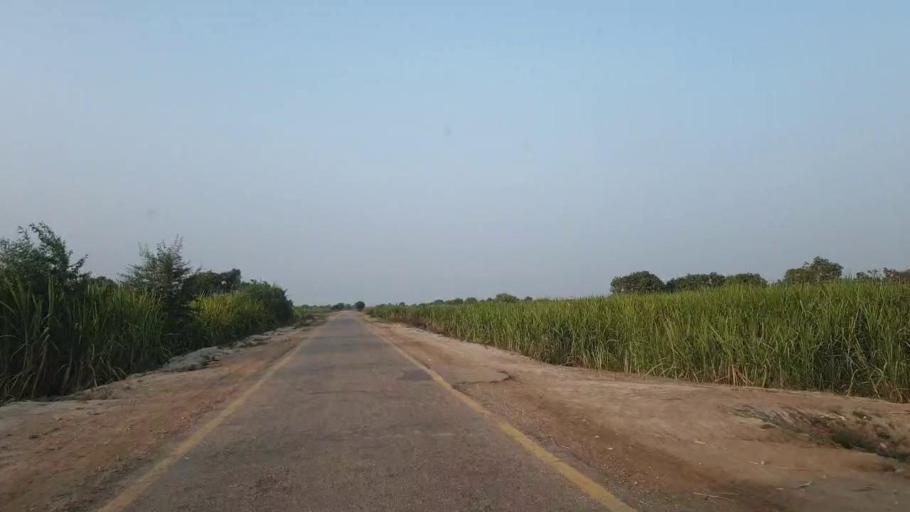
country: PK
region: Sindh
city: Tando Ghulam Ali
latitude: 25.0918
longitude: 68.9586
